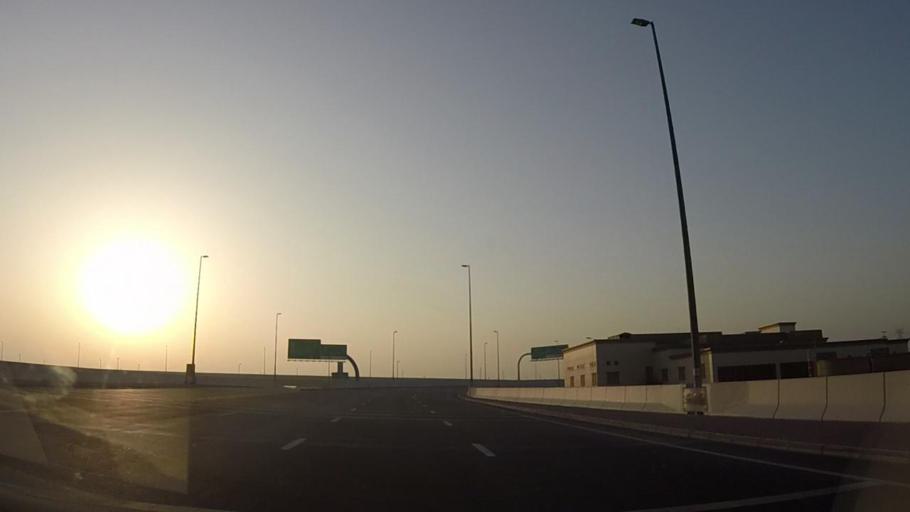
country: AE
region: Dubai
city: Dubai
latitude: 25.0599
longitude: 55.1389
